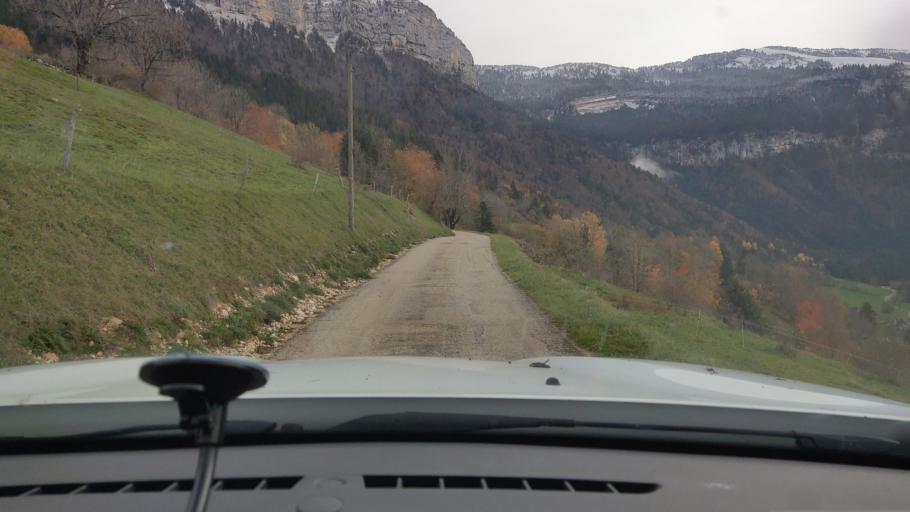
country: FR
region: Rhone-Alpes
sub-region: Departement de l'Isere
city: Saint-Vincent-de-Mercuze
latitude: 45.4135
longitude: 5.8785
